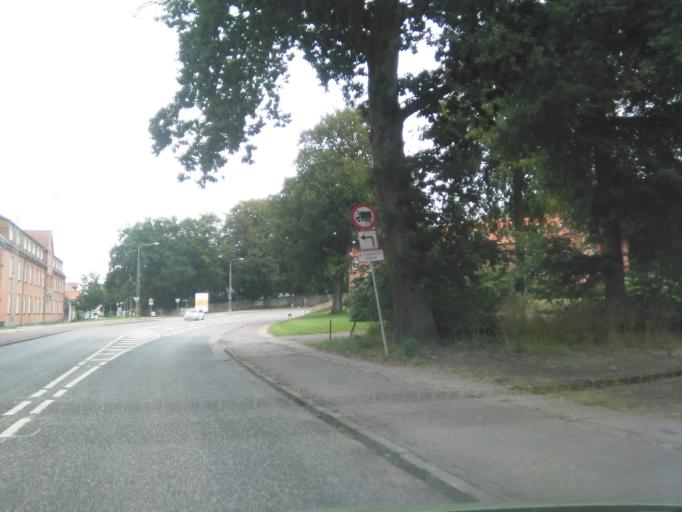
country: DK
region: Central Jutland
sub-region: Odder Kommune
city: Odder
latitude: 55.9681
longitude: 10.1364
